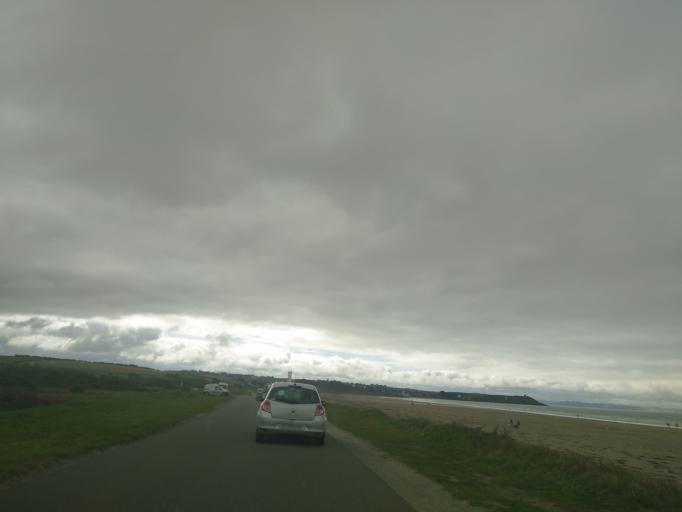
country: FR
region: Brittany
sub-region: Departement du Finistere
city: Plomodiern
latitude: 48.1877
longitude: -4.2984
